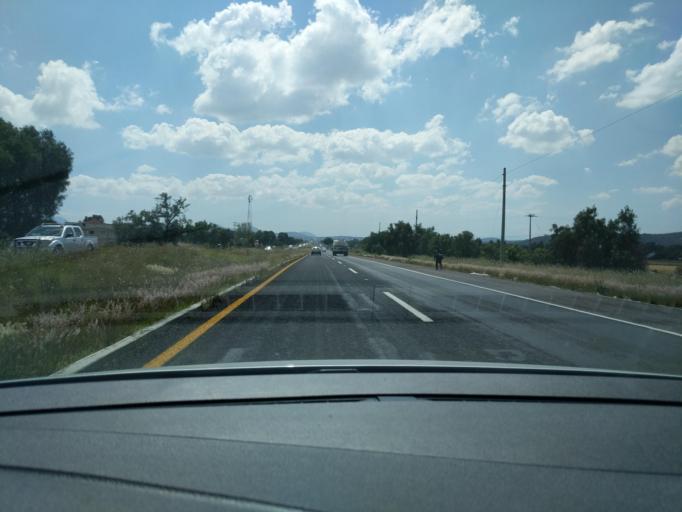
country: MX
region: Hidalgo
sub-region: Mineral de la Reforma
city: Rinconada de los Angeles
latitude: 19.9858
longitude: -98.7043
